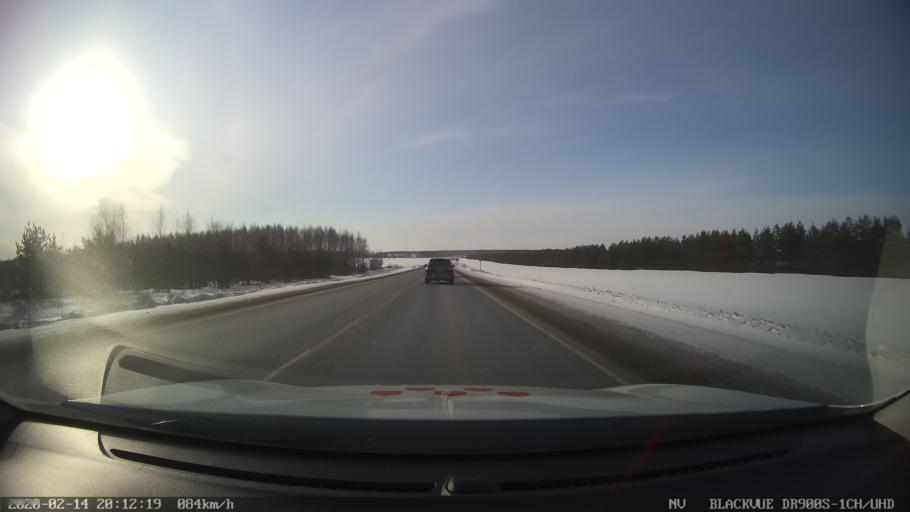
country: RU
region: Tatarstan
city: Verkhniy Uslon
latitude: 55.6672
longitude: 48.8641
